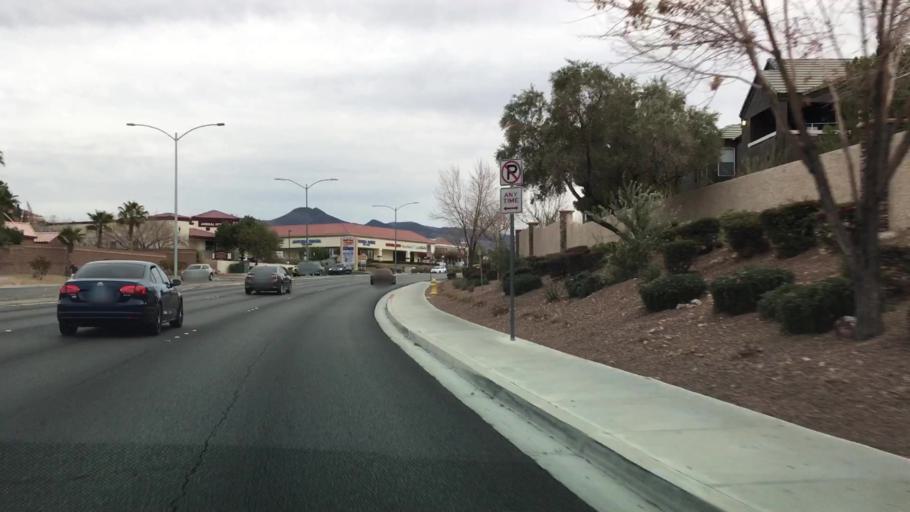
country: US
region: Nevada
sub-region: Clark County
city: Whitney
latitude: 35.9966
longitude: -115.1017
